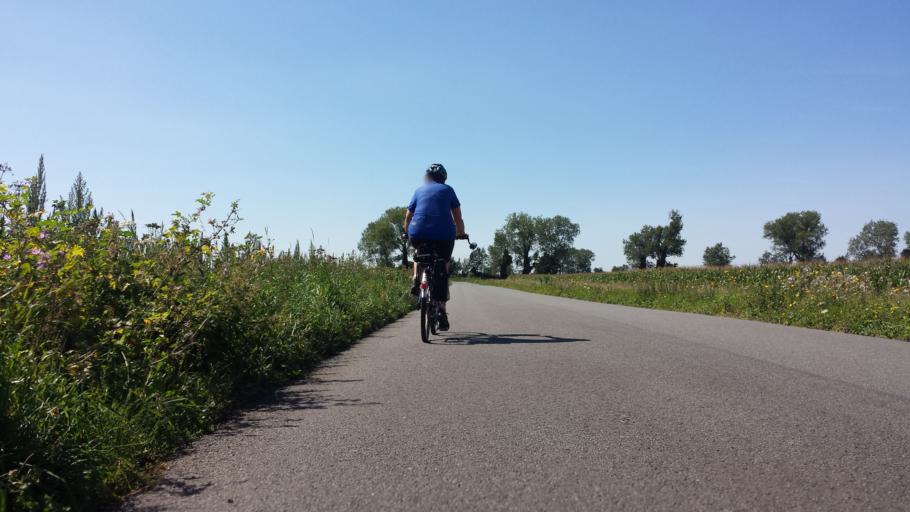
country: GB
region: England
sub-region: Cambridgeshire
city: Isleham
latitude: 52.3459
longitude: 0.3782
